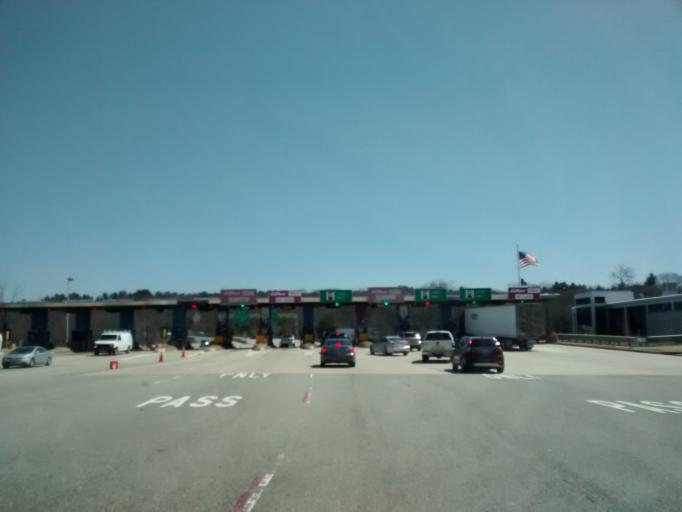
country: US
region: Massachusetts
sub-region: Worcester County
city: Cordaville
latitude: 42.2631
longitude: -71.5676
